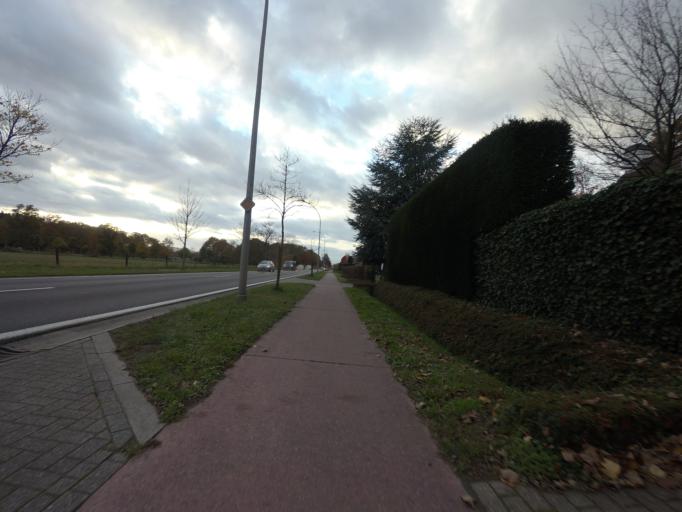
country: BE
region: Flanders
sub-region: Provincie Antwerpen
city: Bonheiden
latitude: 51.0363
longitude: 4.5418
